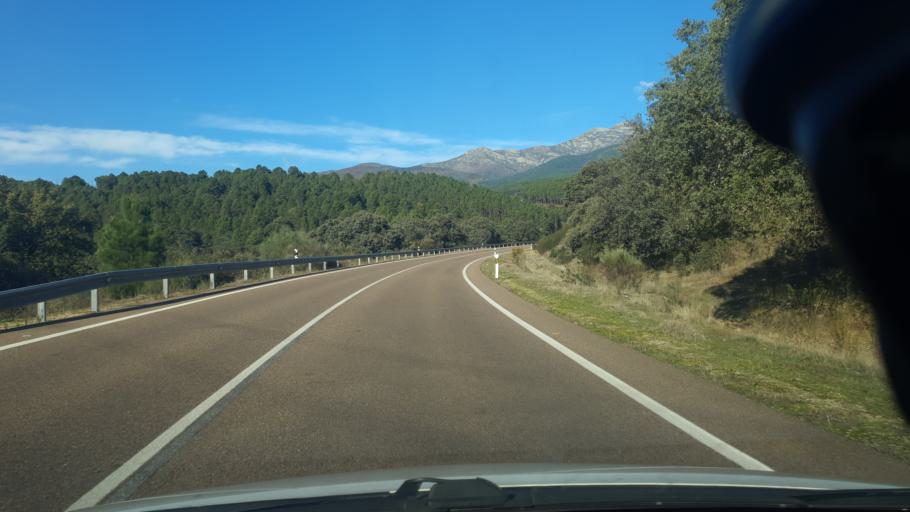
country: ES
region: Castille and Leon
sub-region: Provincia de Avila
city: Poyales del Hoyo
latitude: 40.1635
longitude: -5.1186
